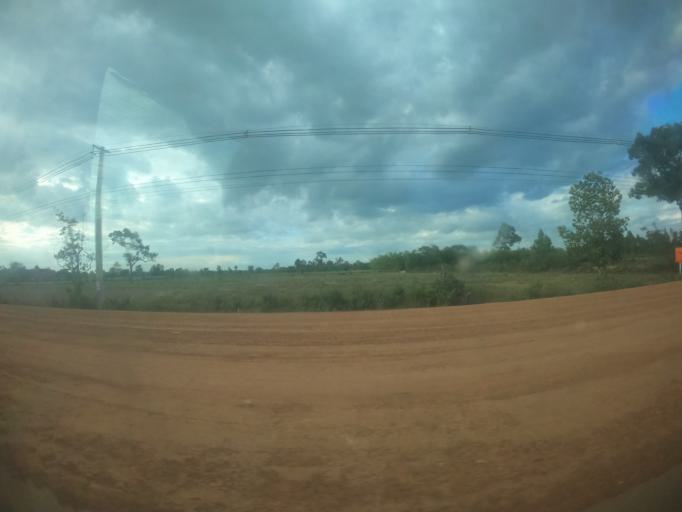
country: TH
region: Surin
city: Kap Choeng
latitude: 14.4580
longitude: 103.6705
